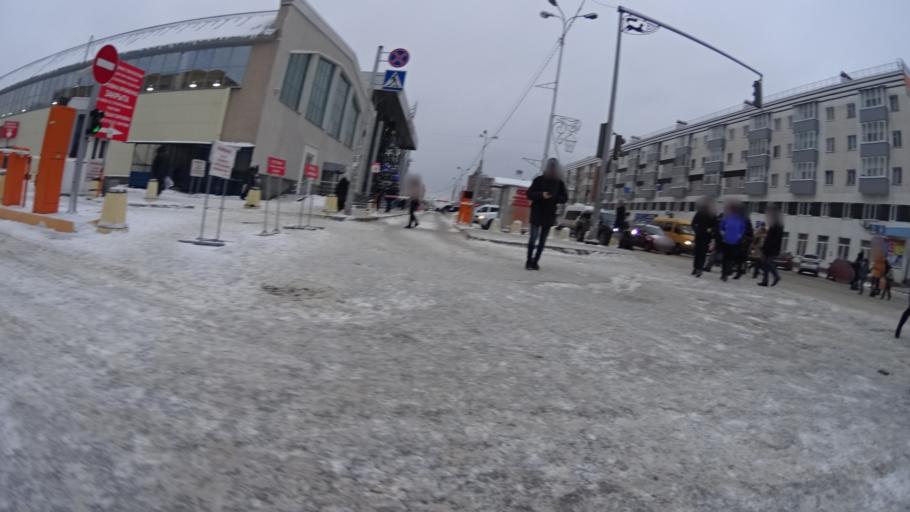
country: RU
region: Bashkortostan
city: Ufa
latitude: 54.7354
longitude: 55.9578
